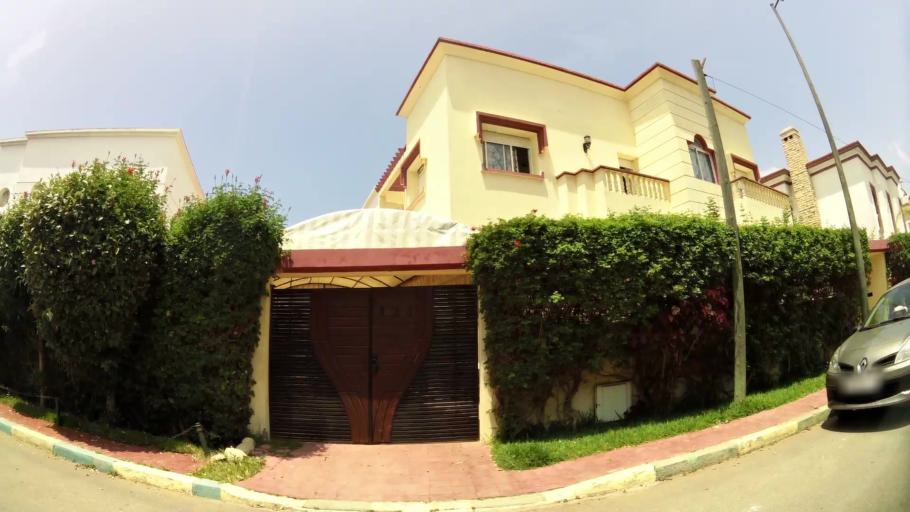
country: MA
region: Rabat-Sale-Zemmour-Zaer
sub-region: Skhirate-Temara
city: Temara
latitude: 33.9695
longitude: -6.9032
